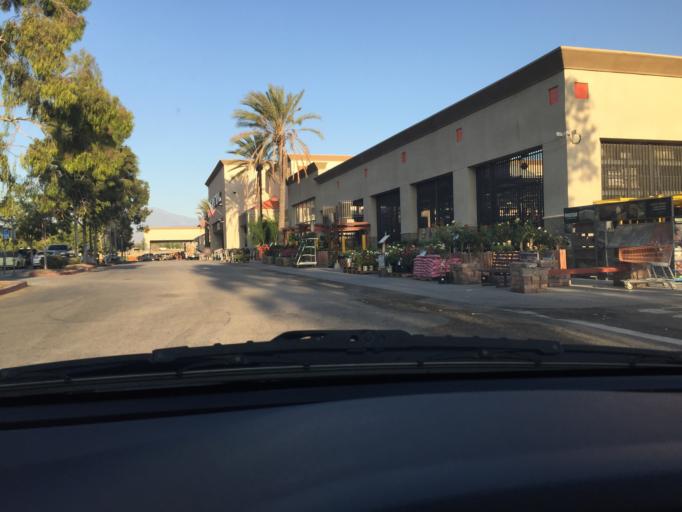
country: US
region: California
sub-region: San Bernardino County
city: Redlands
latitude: 34.0688
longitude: -117.1989
